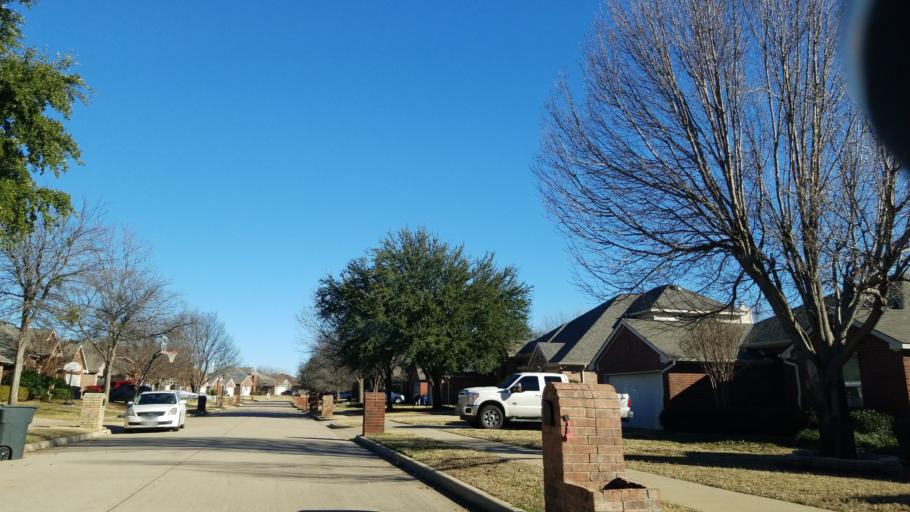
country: US
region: Texas
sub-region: Denton County
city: Corinth
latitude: 33.1370
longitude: -97.0870
